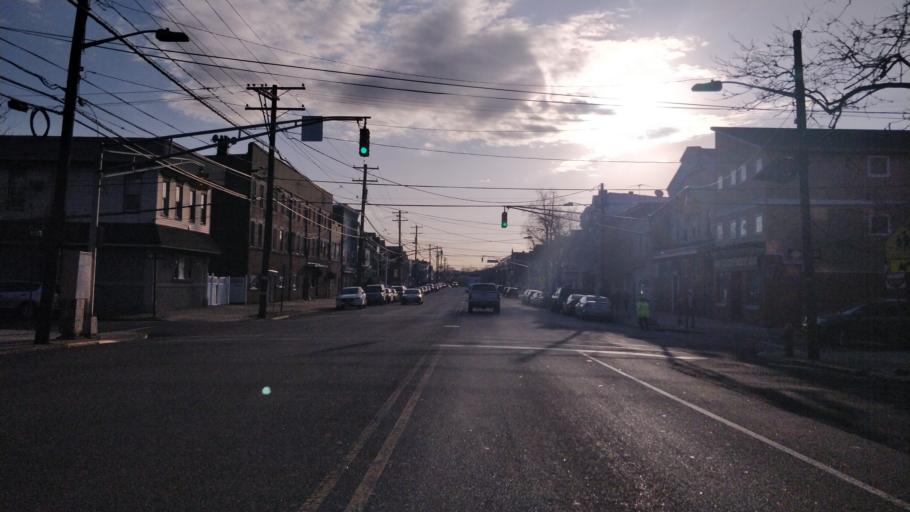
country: US
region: New Jersey
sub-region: Hudson County
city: Bayonne
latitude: 40.6583
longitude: -74.1264
